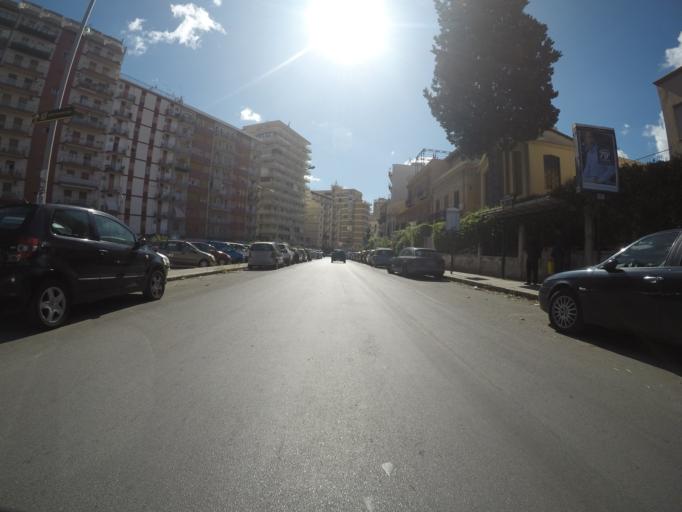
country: IT
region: Sicily
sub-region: Palermo
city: Palermo
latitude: 38.1428
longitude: 13.3571
